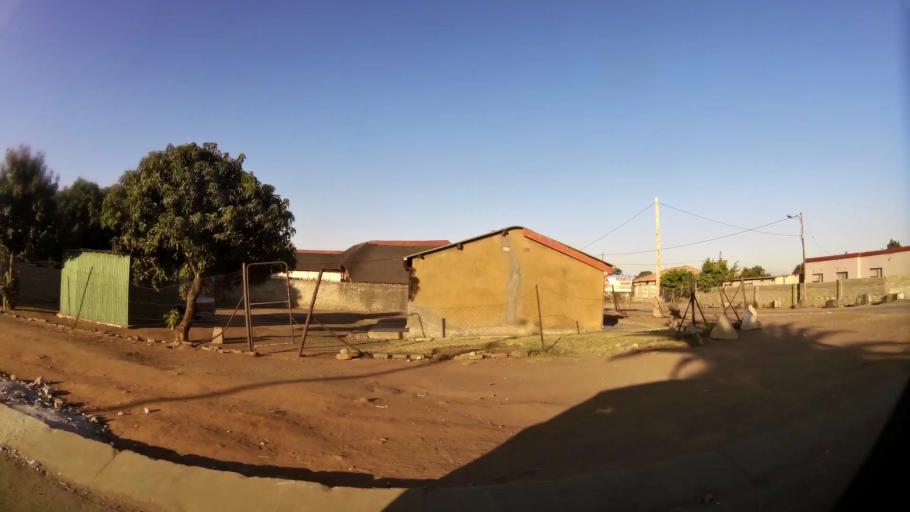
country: ZA
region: North-West
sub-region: Bojanala Platinum District Municipality
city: Rustenburg
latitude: -25.6284
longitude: 27.2155
